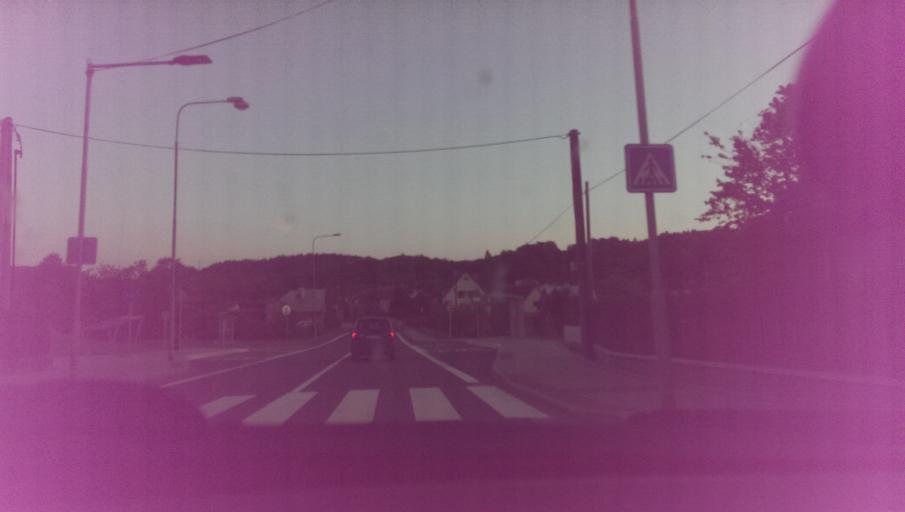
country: CZ
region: Zlin
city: Valasska Polanka
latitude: 49.2694
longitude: 17.9972
